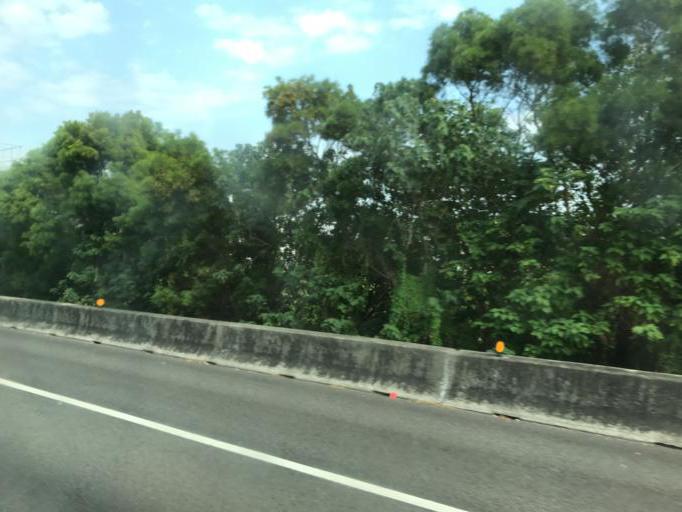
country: TW
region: Taiwan
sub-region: Hsinchu
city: Zhubei
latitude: 24.8080
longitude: 121.0104
